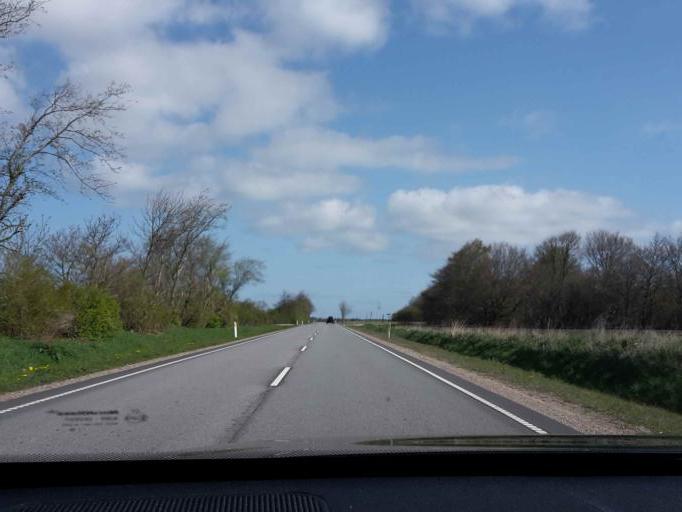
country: DK
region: South Denmark
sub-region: Billund Kommune
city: Grindsted
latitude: 55.6465
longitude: 8.9545
